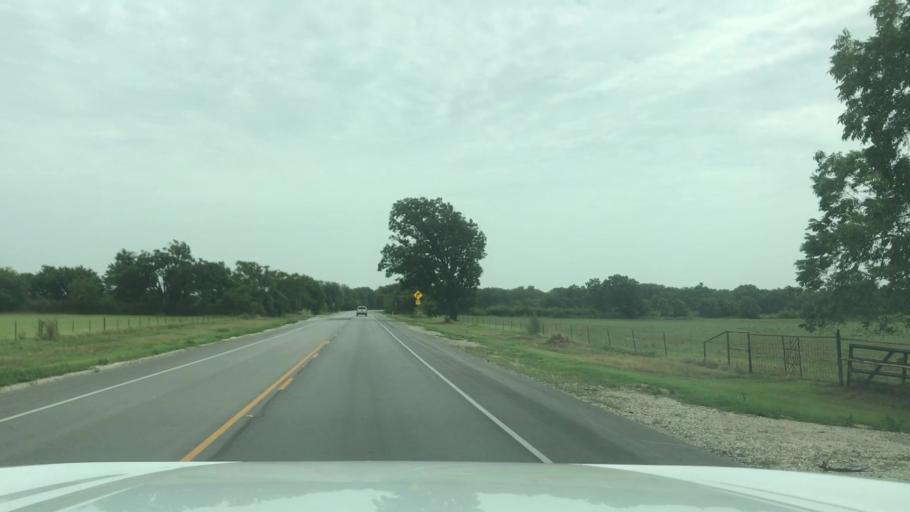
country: US
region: Texas
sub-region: Erath County
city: Dublin
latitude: 32.0914
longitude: -98.2740
